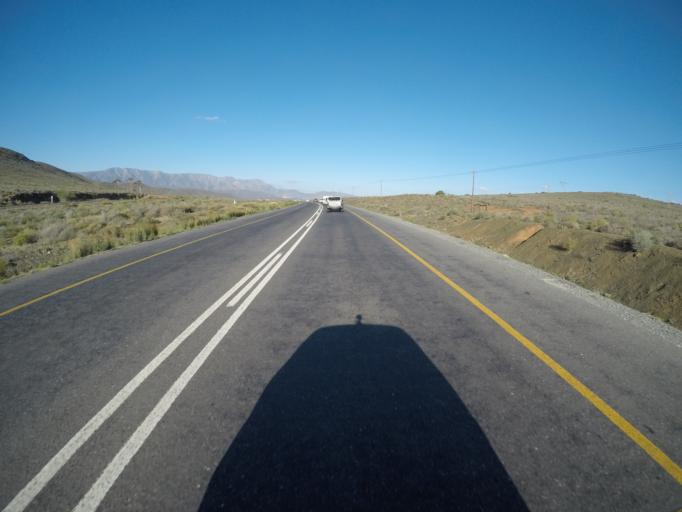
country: ZA
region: Western Cape
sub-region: Cape Winelands District Municipality
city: Worcester
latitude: -33.7348
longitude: 19.6550
